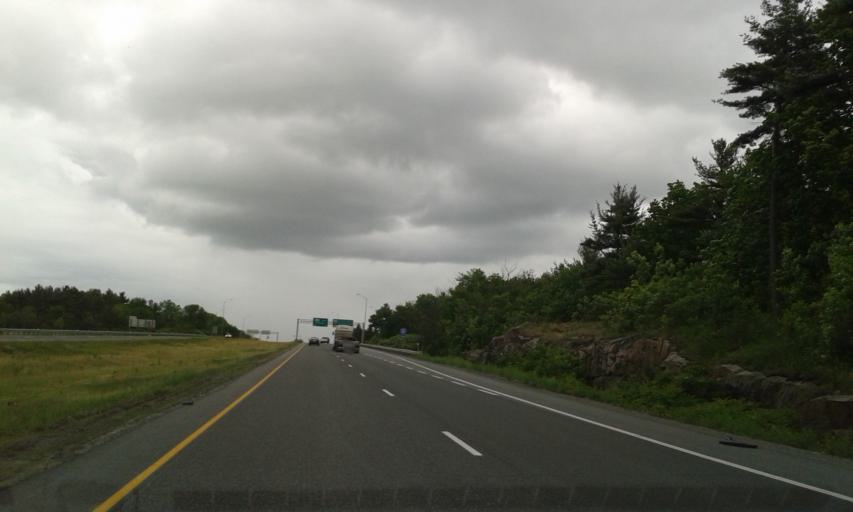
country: US
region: New York
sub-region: Jefferson County
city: Alexandria Bay
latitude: 44.3800
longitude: -75.9917
